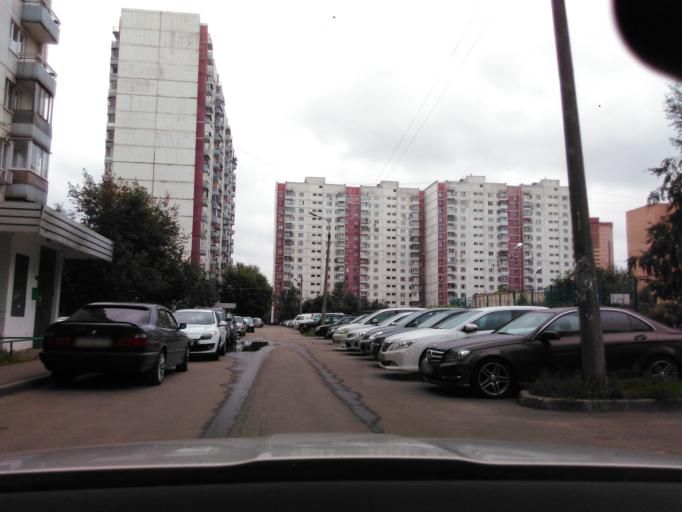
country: RU
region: Moscow
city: Khimki
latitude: 55.9039
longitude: 37.4055
